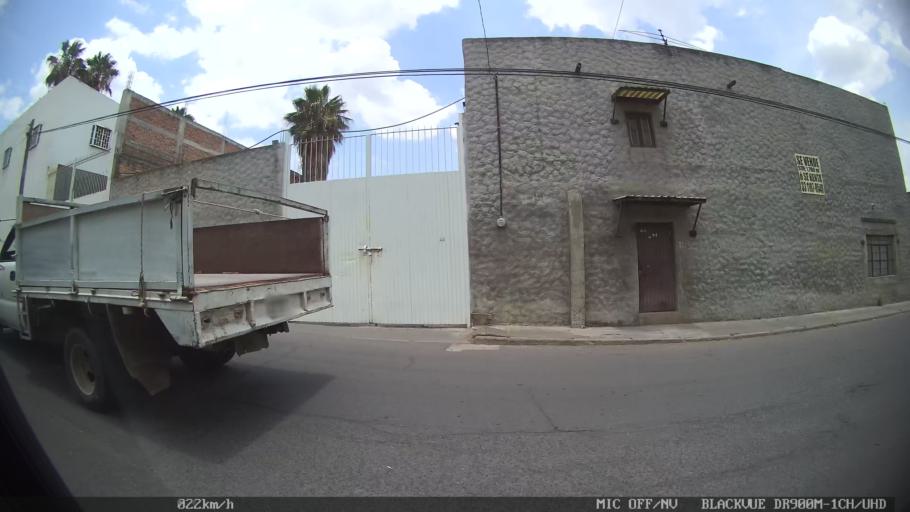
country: MX
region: Jalisco
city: Tonala
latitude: 20.6587
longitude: -103.2262
